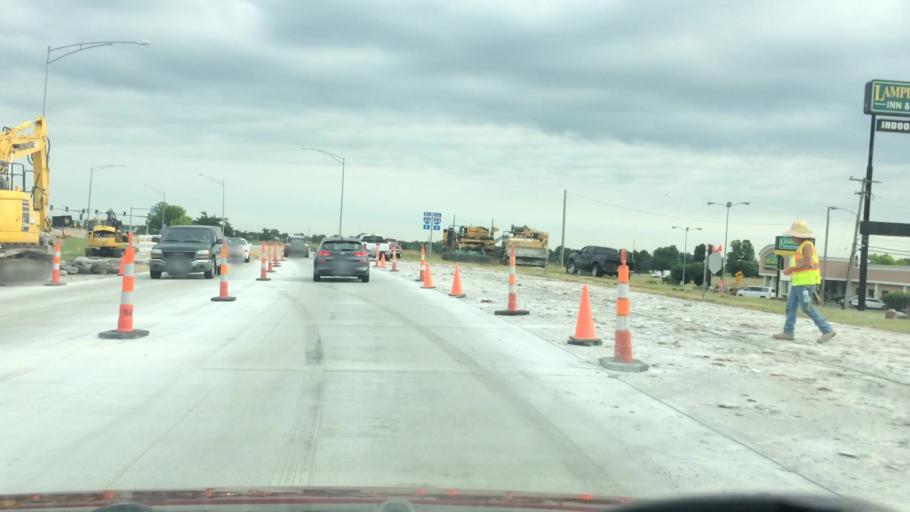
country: US
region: Missouri
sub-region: Greene County
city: Springfield
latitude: 37.2467
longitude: -93.2608
